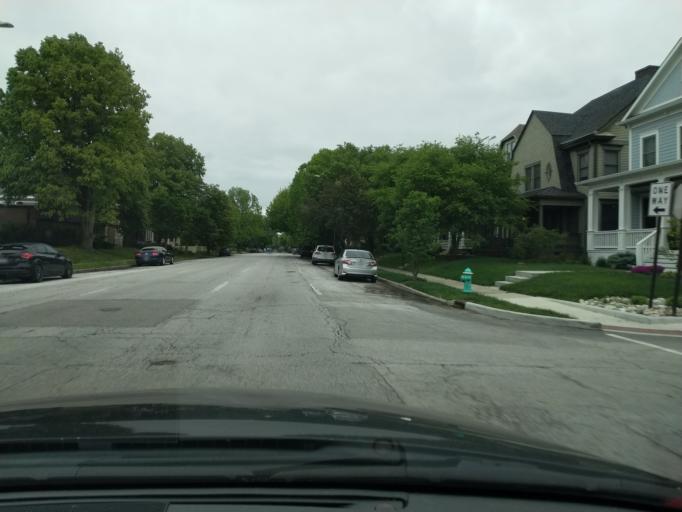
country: US
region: Indiana
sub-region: Marion County
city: Indianapolis
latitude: 39.7926
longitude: -86.1537
